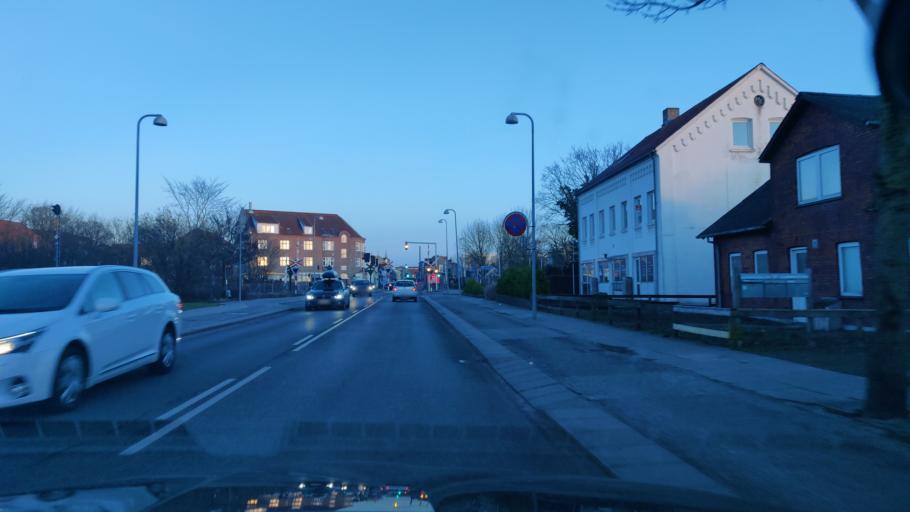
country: DK
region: North Denmark
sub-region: Alborg Kommune
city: Aalborg
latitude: 57.0630
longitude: 9.9101
